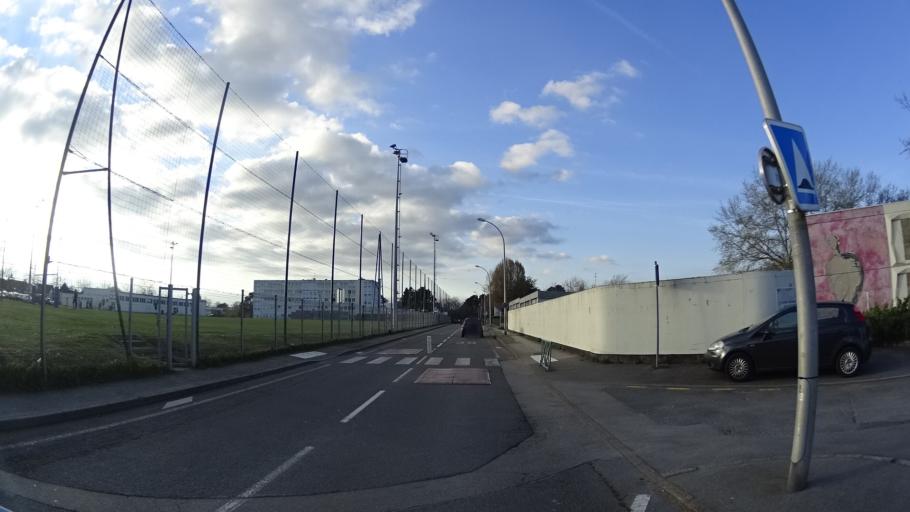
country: FR
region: Brittany
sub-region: Departement du Morbihan
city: Vannes
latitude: 47.6452
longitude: -2.7770
